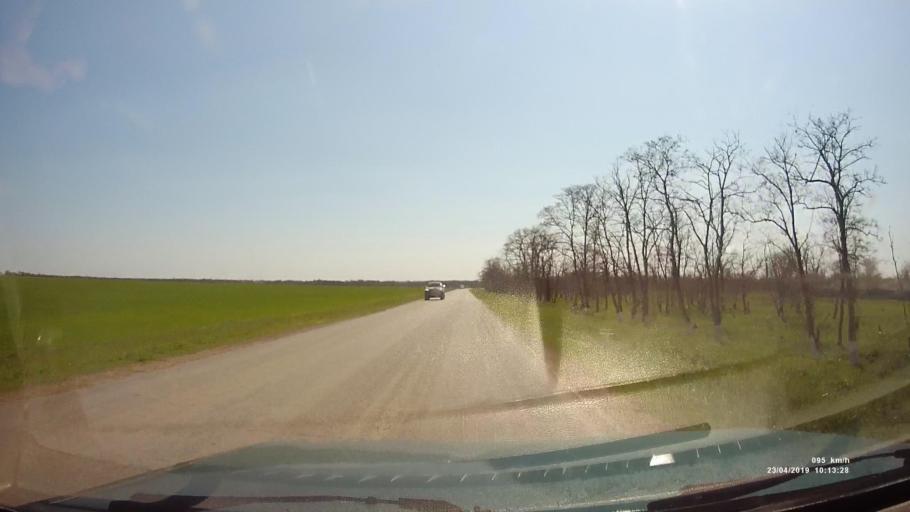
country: RU
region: Rostov
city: Sovetskoye
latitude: 46.6846
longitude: 42.3559
